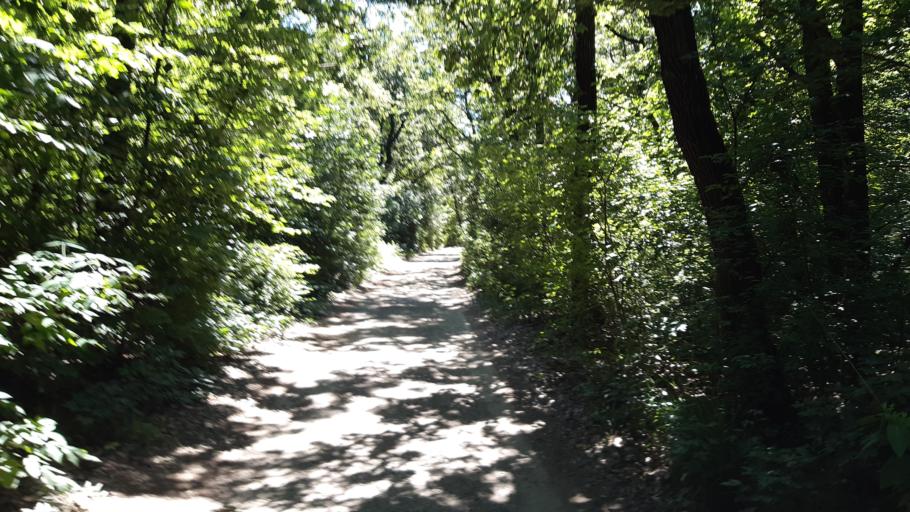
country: HU
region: Pest
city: Budaors
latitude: 47.4795
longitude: 18.9615
